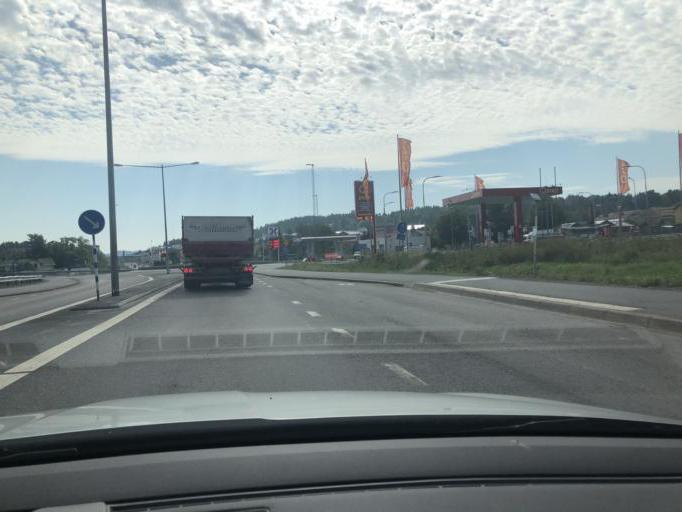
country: SE
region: Vaesternorrland
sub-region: Kramfors Kommun
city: Kramfors
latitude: 62.9355
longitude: 17.7708
